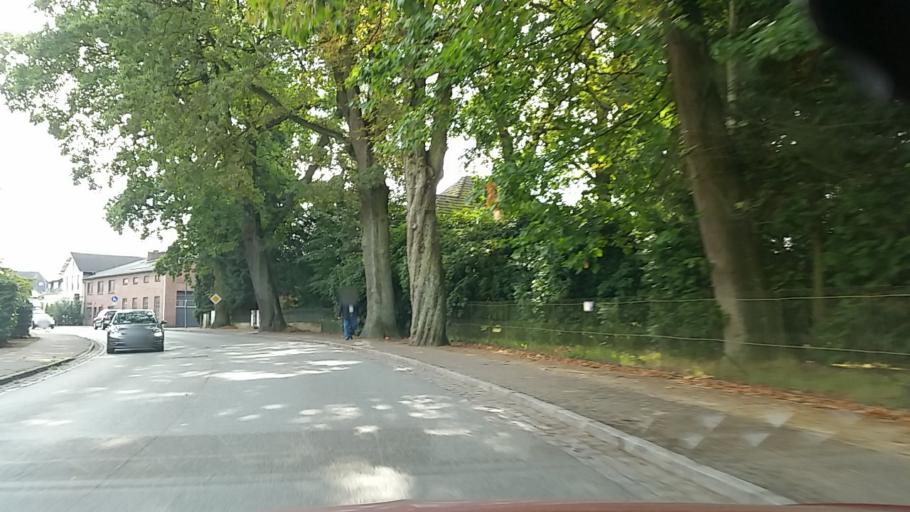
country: DE
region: Schleswig-Holstein
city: Halstenbek
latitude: 53.6022
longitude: 9.8190
